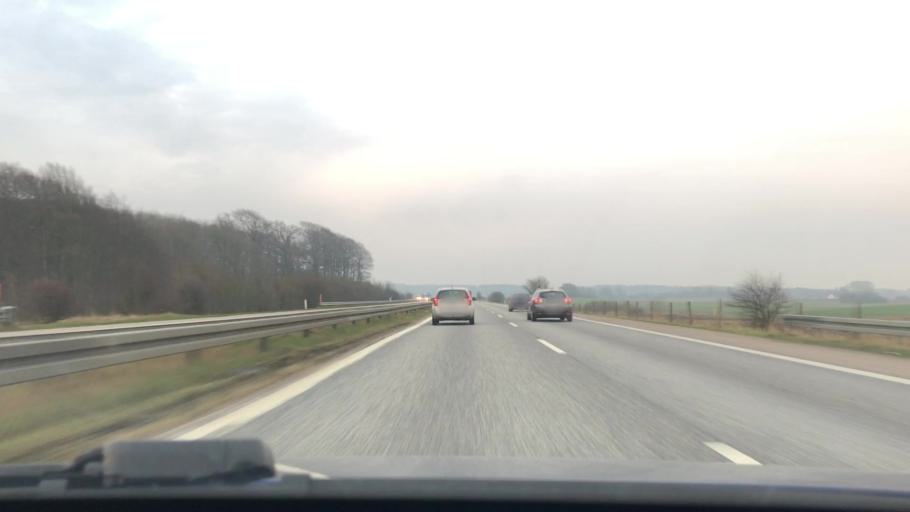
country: DK
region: South Denmark
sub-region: Kolding Kommune
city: Christiansfeld
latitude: 55.3230
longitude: 9.4379
